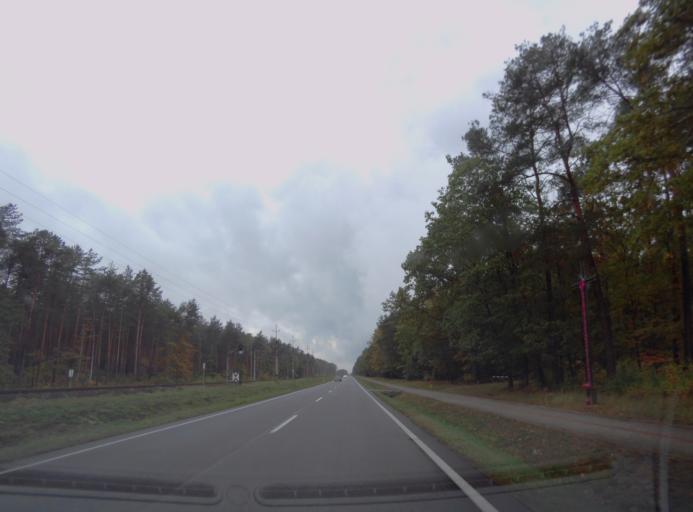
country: PL
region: Subcarpathian Voivodeship
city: Nowa Sarzyna
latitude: 50.3073
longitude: 22.3621
